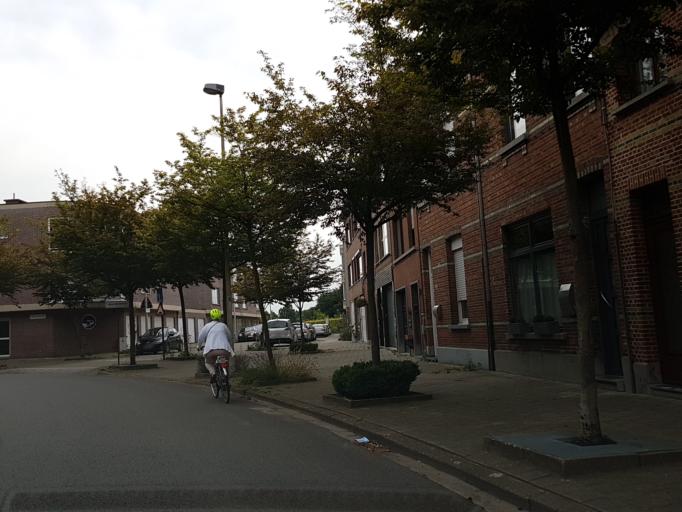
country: BE
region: Flanders
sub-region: Provincie Antwerpen
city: Borsbeek
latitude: 51.1988
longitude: 4.4701
